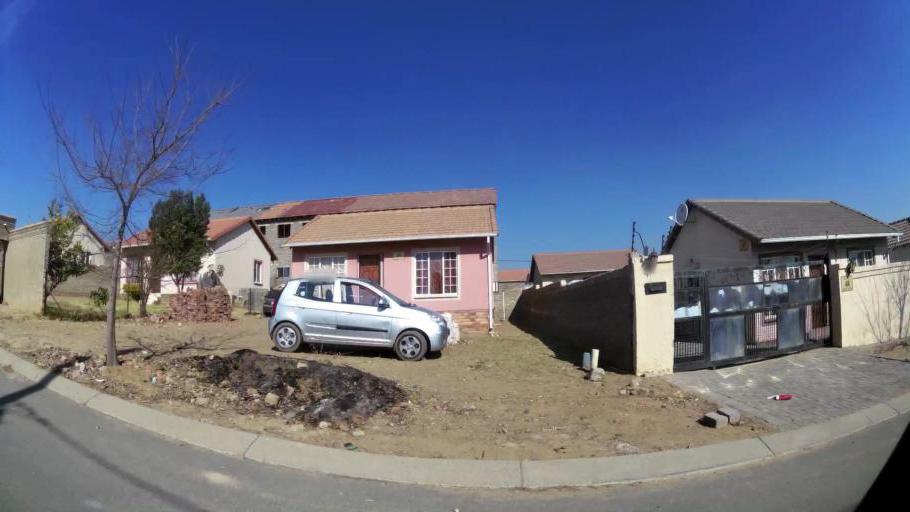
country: ZA
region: Gauteng
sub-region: West Rand District Municipality
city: Muldersdriseloop
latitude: -26.0346
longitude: 27.9209
